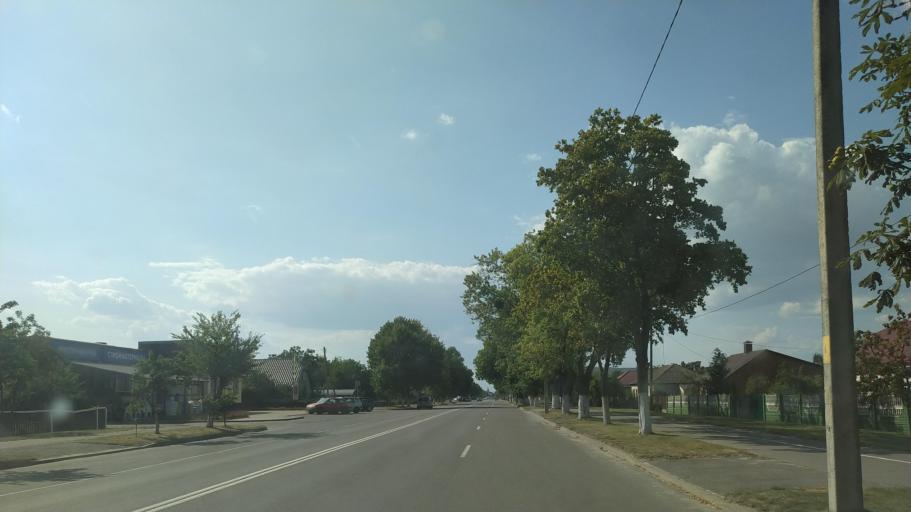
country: BY
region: Brest
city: Drahichyn
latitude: 52.1845
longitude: 25.1691
